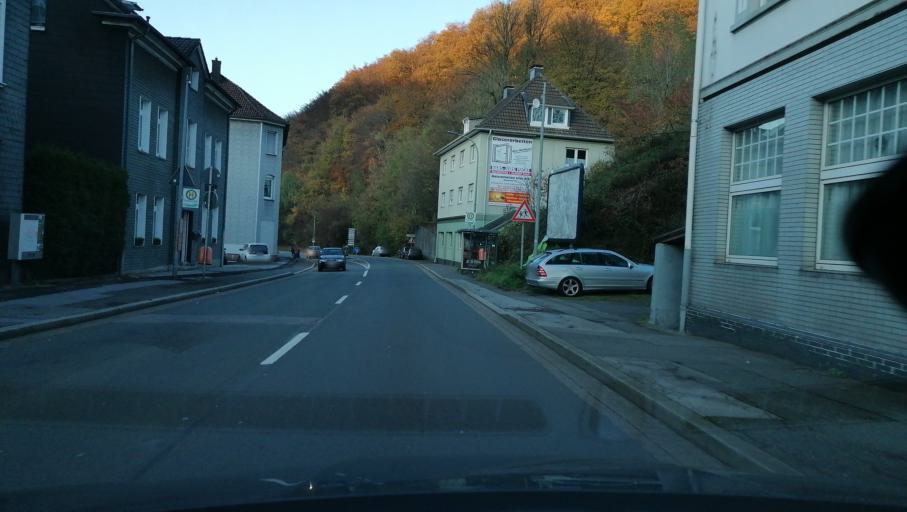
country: DE
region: North Rhine-Westphalia
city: Ennepetal
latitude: 51.2917
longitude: 7.3426
